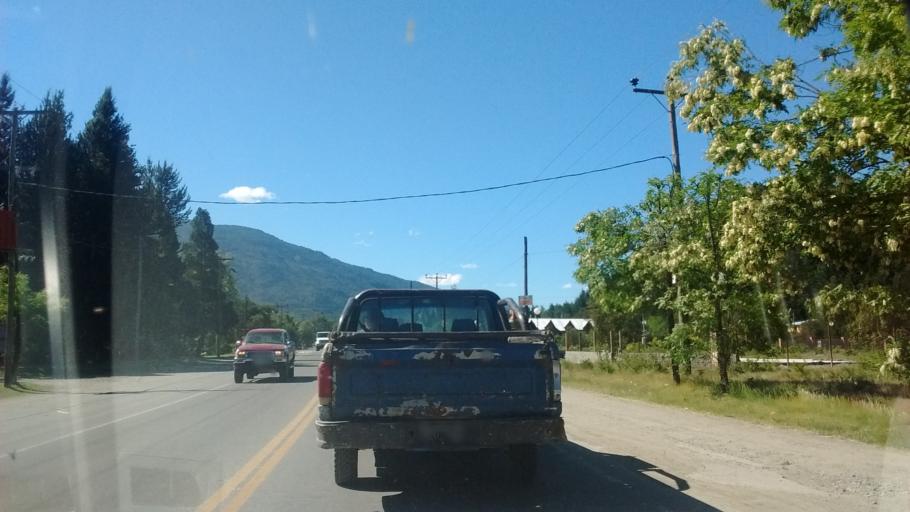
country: AR
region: Chubut
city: Lago Puelo
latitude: -42.0566
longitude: -71.5963
